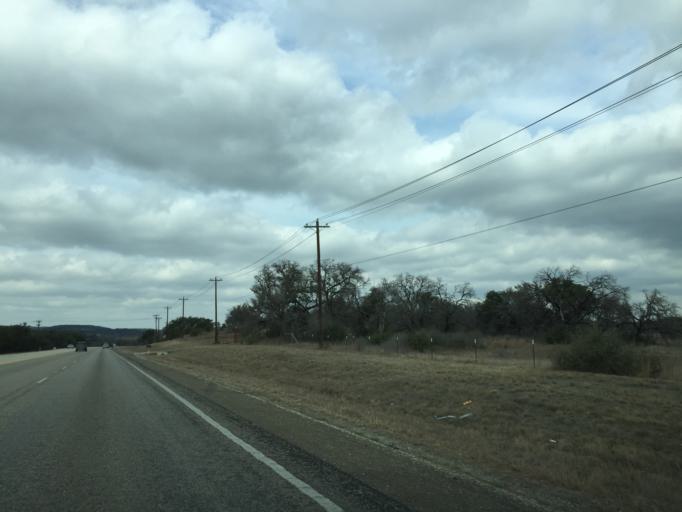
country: US
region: Texas
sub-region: Travis County
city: Briarcliff
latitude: 30.4157
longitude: -98.1190
